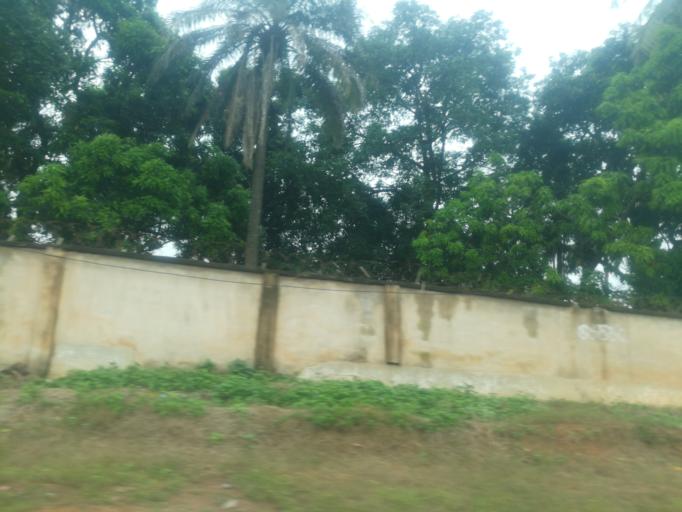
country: NG
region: Oyo
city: Ibadan
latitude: 7.3931
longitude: 3.9254
